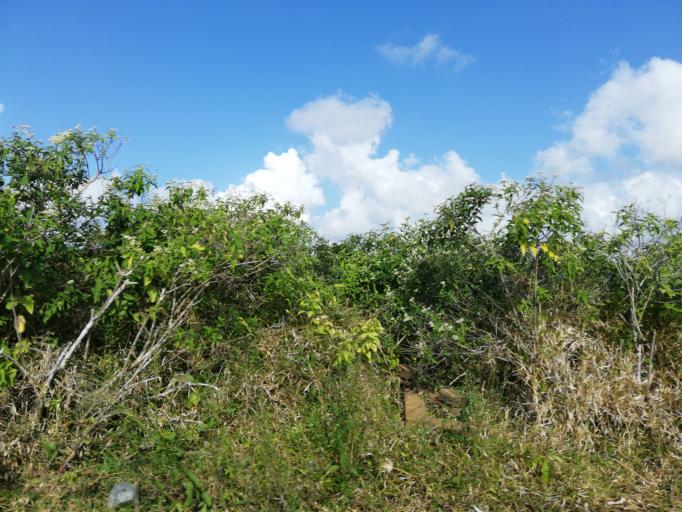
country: MU
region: Moka
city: Verdun
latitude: -20.2263
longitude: 57.5491
